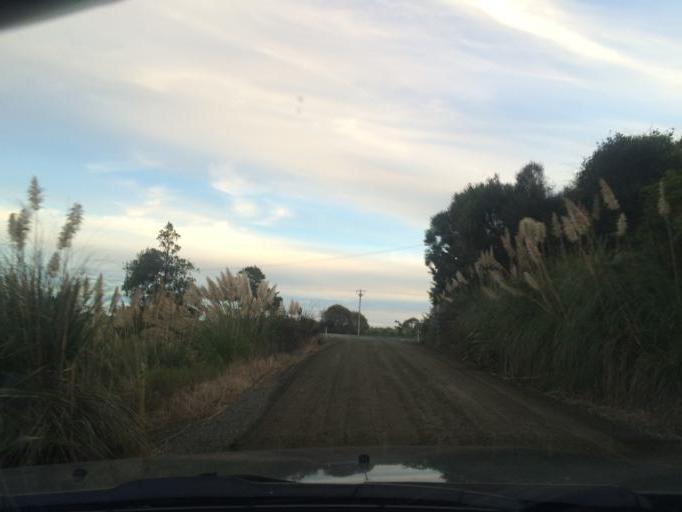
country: NZ
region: Northland
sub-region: Whangarei
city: Maungatapere
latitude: -35.8195
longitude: 174.0401
